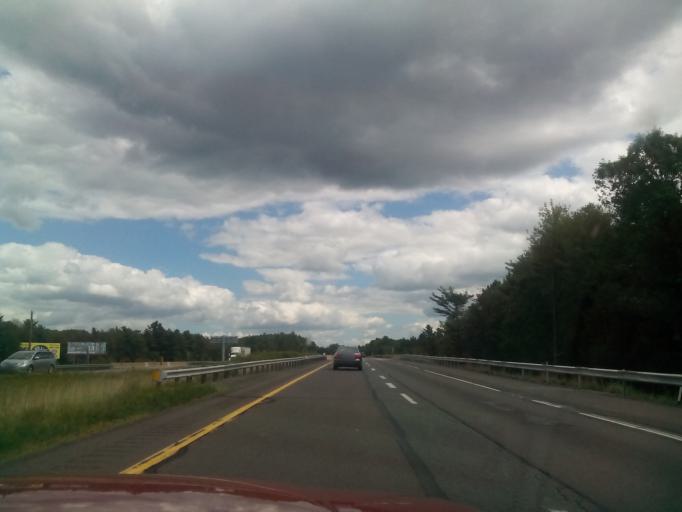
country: US
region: Pennsylvania
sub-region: Monroe County
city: Pocono Pines
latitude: 41.0770
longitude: -75.5075
